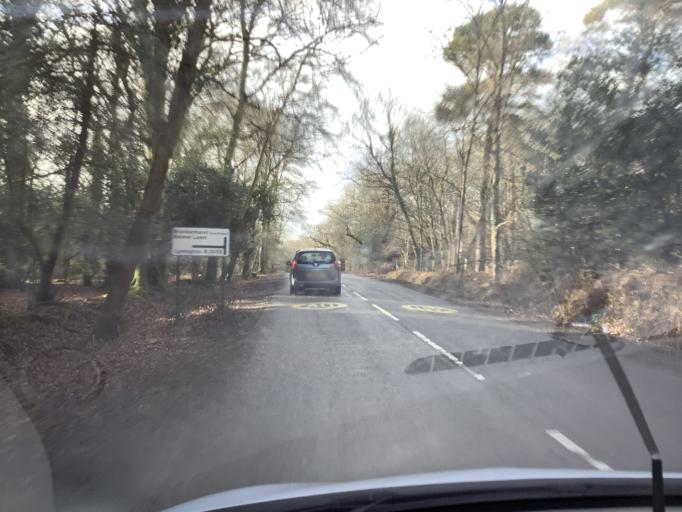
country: GB
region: England
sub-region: Hampshire
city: Brockenhurst
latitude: 50.8213
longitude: -1.5528
